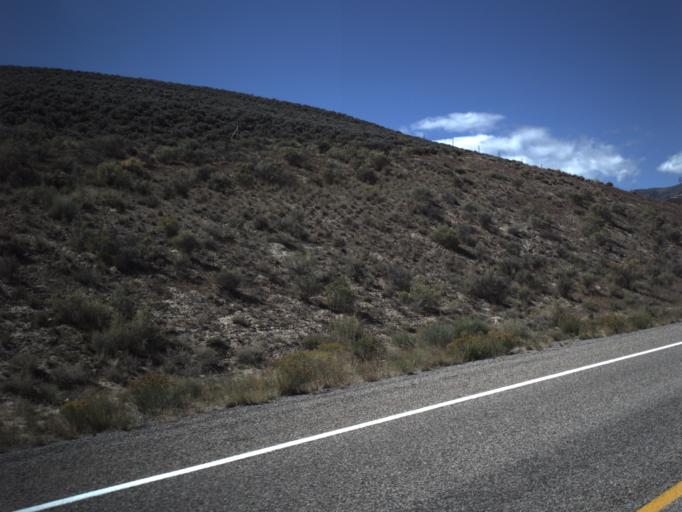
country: US
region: Utah
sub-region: Piute County
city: Junction
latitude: 38.2092
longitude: -112.2153
